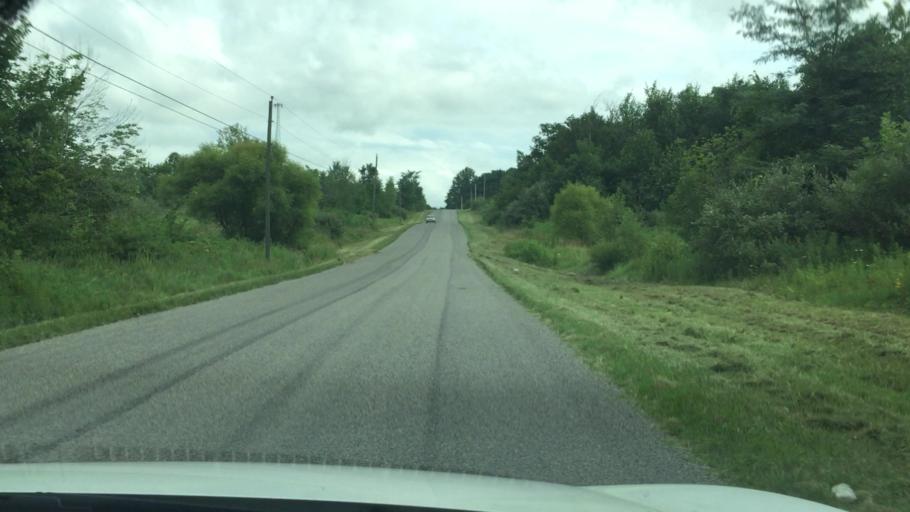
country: US
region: Ohio
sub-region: Champaign County
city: North Lewisburg
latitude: 40.2638
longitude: -83.5354
